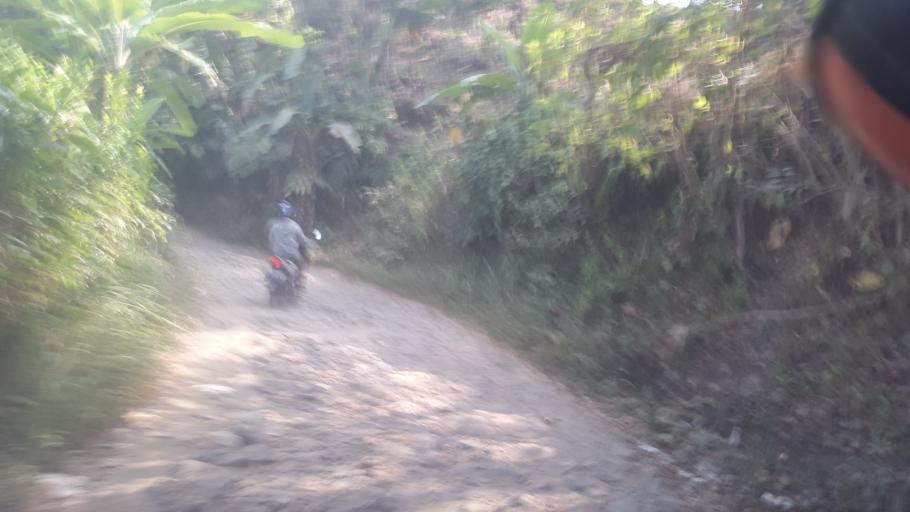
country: ID
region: West Java
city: Tugu
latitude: -6.9436
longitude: 106.4466
